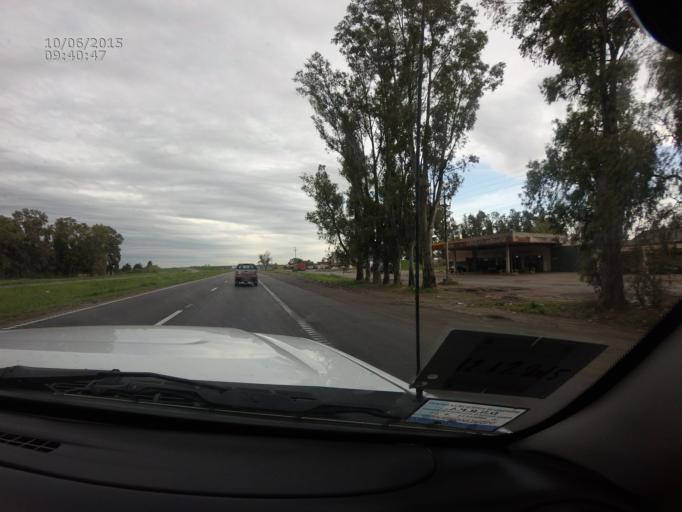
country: AR
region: Buenos Aires
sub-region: Partido de Zarate
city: Zarate
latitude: -34.0821
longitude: -59.2045
